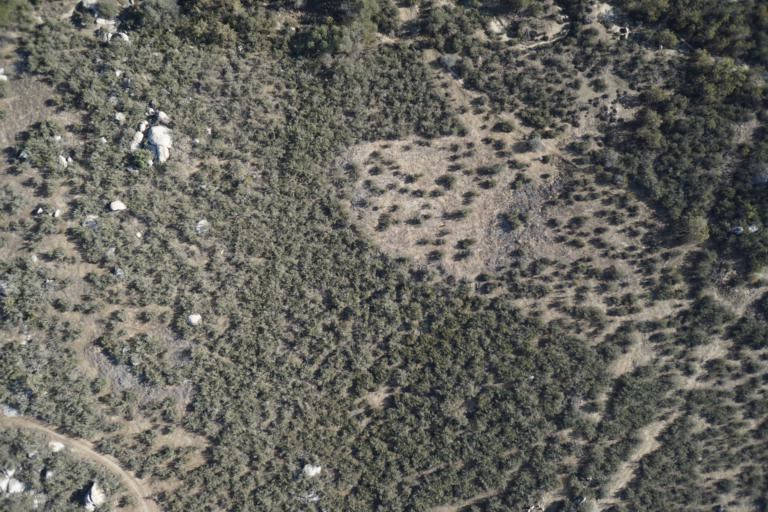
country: US
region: California
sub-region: Riverside County
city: Valle Vista
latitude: 33.6285
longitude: -116.8879
